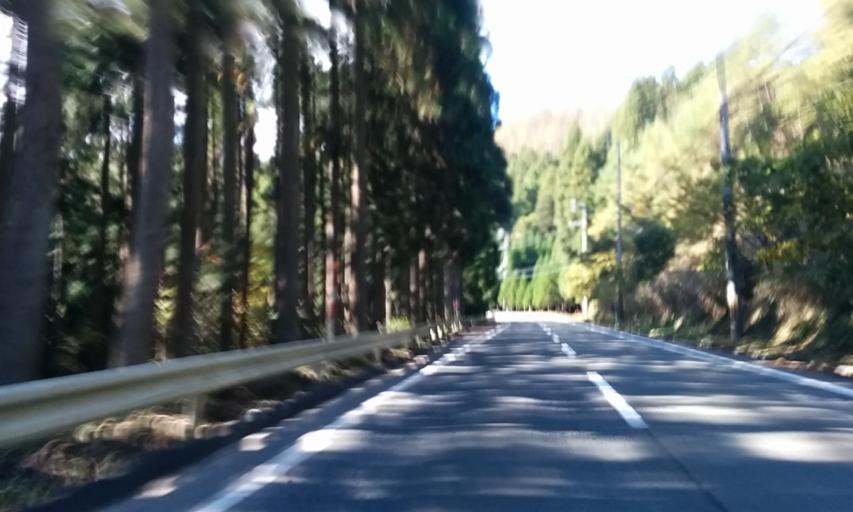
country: JP
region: Kyoto
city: Kameoka
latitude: 35.2003
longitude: 135.6225
